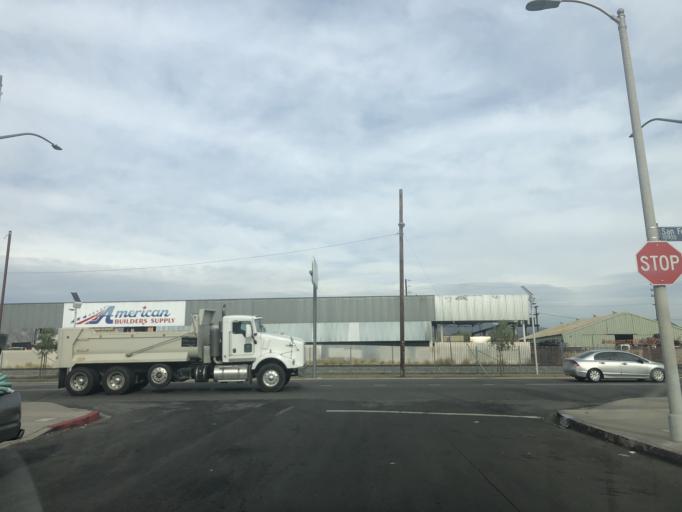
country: US
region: California
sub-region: Los Angeles County
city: San Fernando
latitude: 34.2697
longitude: -118.4264
